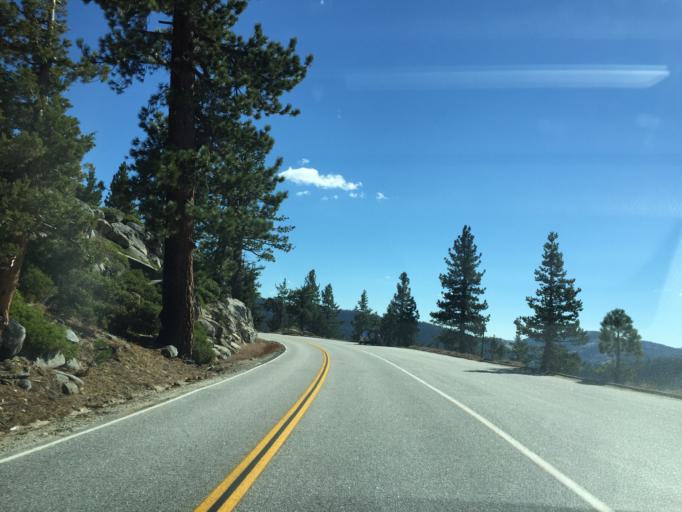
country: US
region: California
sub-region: Mariposa County
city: Yosemite Valley
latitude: 37.8444
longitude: -119.5952
